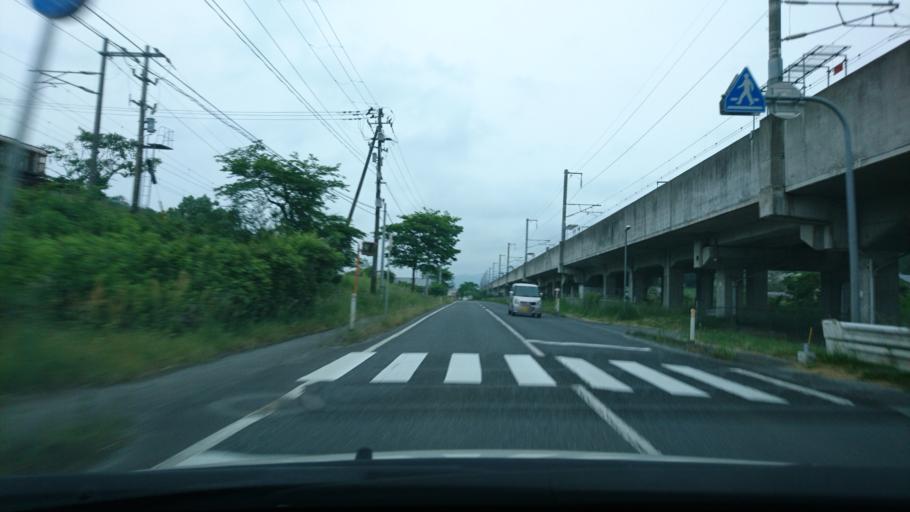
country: JP
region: Iwate
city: Ichinoseki
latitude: 38.9036
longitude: 141.1301
